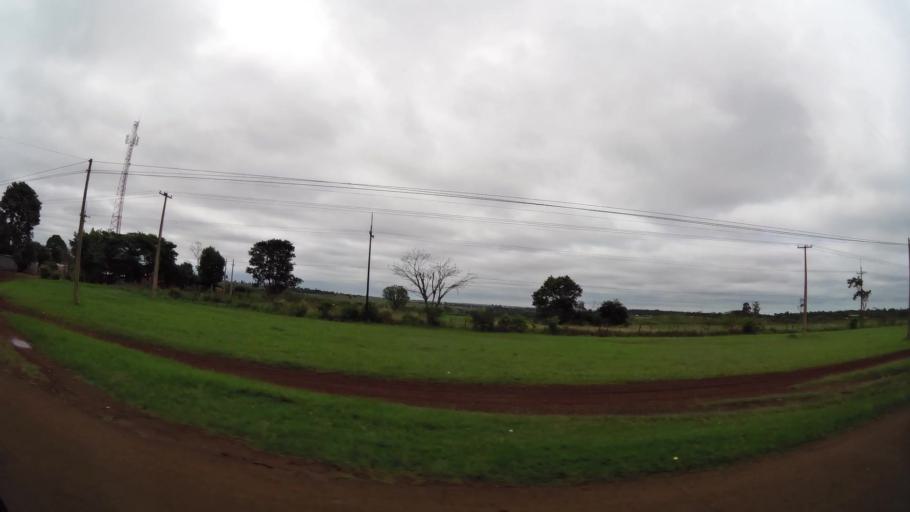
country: PY
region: Alto Parana
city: Colonia Yguazu
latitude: -25.4870
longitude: -54.8490
